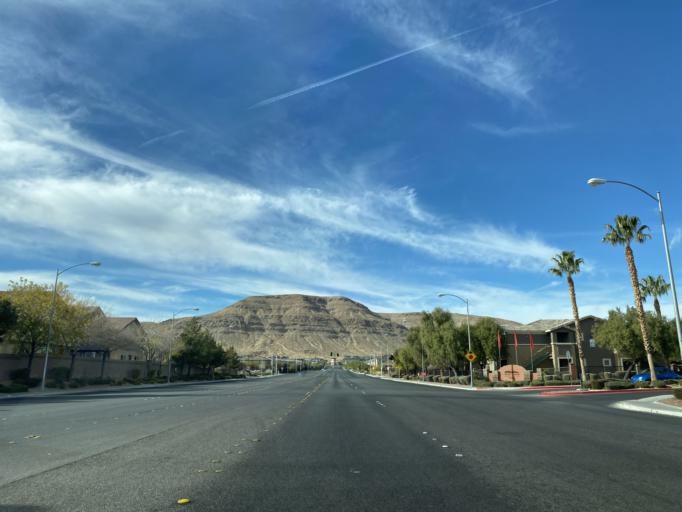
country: US
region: Nevada
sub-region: Clark County
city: Summerlin South
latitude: 36.0702
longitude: -115.3041
